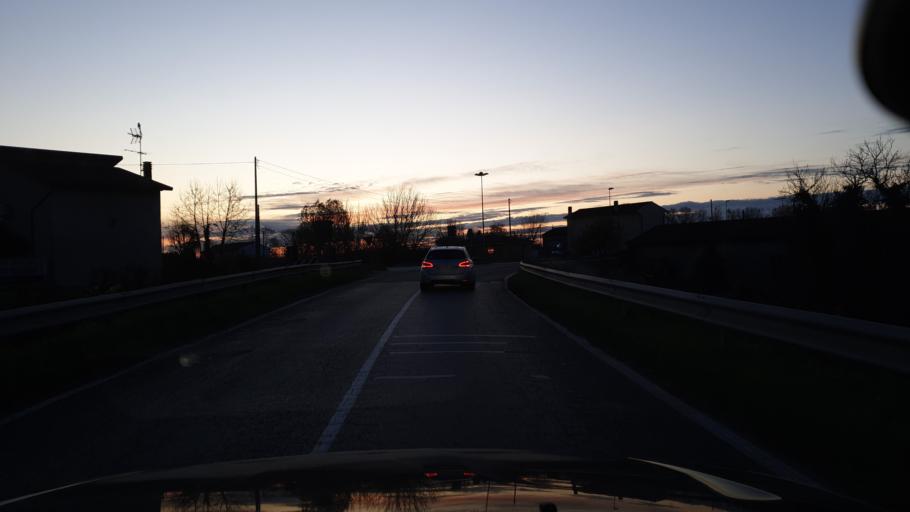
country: IT
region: Veneto
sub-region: Provincia di Rovigo
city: Fratta Polesine
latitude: 45.0203
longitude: 11.6382
